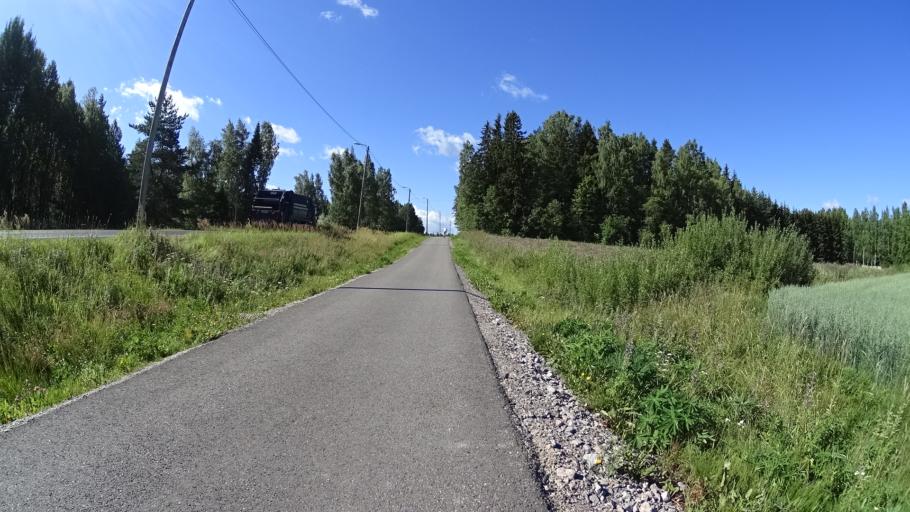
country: FI
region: Uusimaa
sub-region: Helsinki
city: Jaervenpaeae
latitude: 60.4366
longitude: 25.0666
